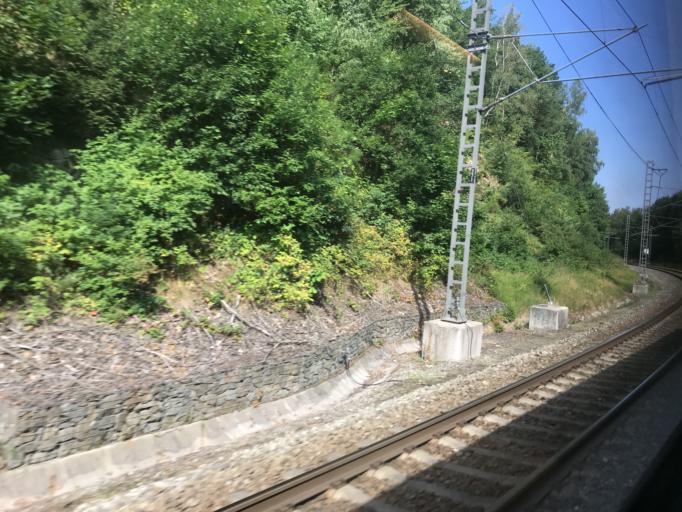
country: CZ
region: Central Bohemia
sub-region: Okres Benesov
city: Cercany
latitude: 49.8273
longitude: 14.7032
